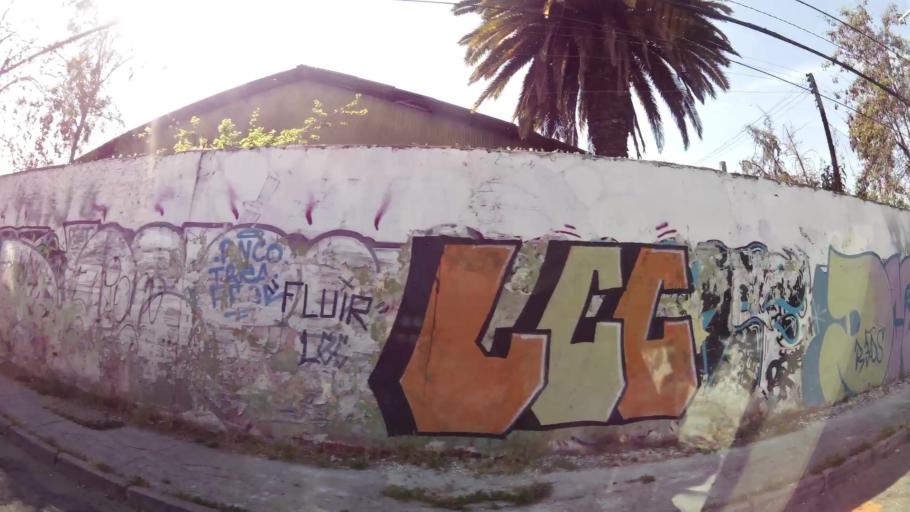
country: CL
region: Santiago Metropolitan
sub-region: Provincia de Santiago
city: La Pintana
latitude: -33.5564
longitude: -70.6663
